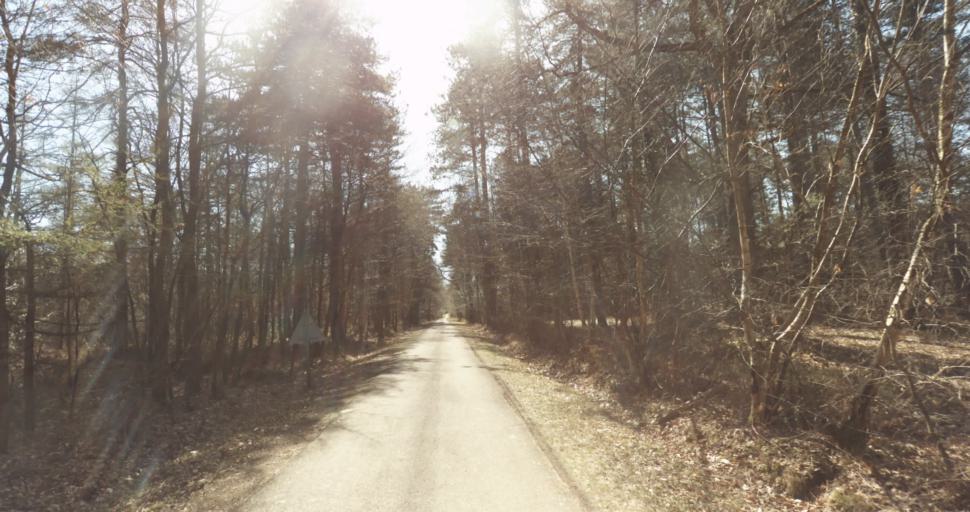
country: FR
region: Lower Normandy
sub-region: Departement du Calvados
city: Livarot
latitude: 49.0032
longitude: 0.0580
